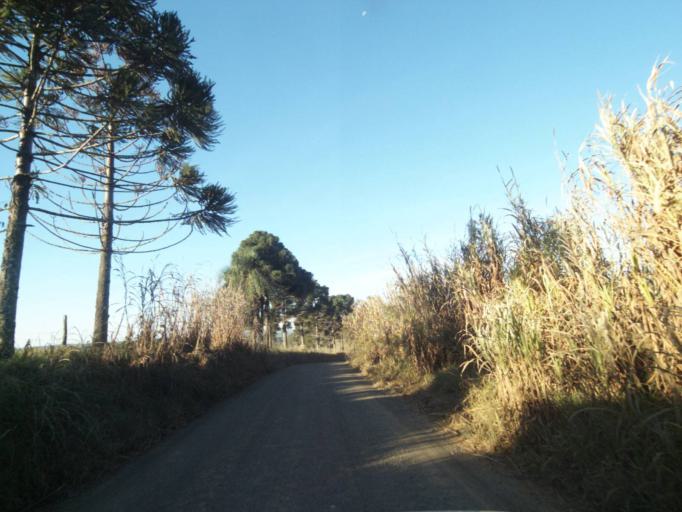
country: BR
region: Parana
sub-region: Telemaco Borba
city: Telemaco Borba
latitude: -24.4267
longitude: -50.5953
